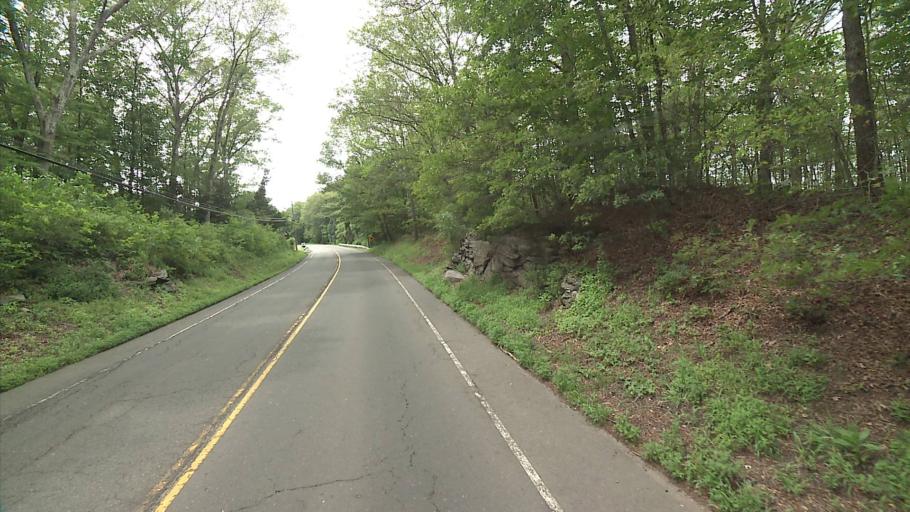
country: US
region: Connecticut
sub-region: Middlesex County
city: Clinton
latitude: 41.3577
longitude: -72.5451
